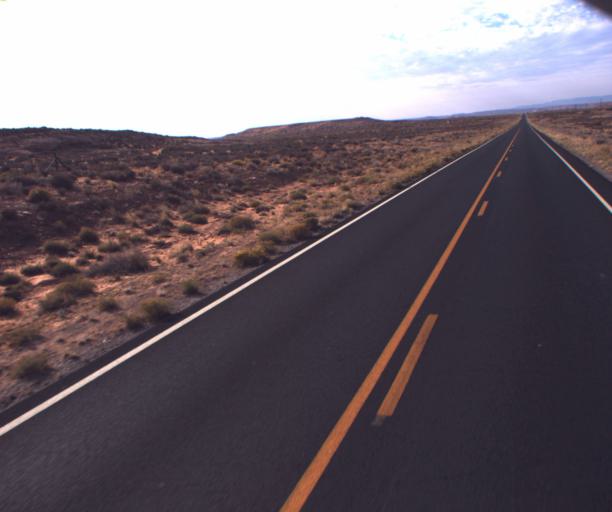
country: US
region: Arizona
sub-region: Apache County
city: Many Farms
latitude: 36.8817
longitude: -109.6290
